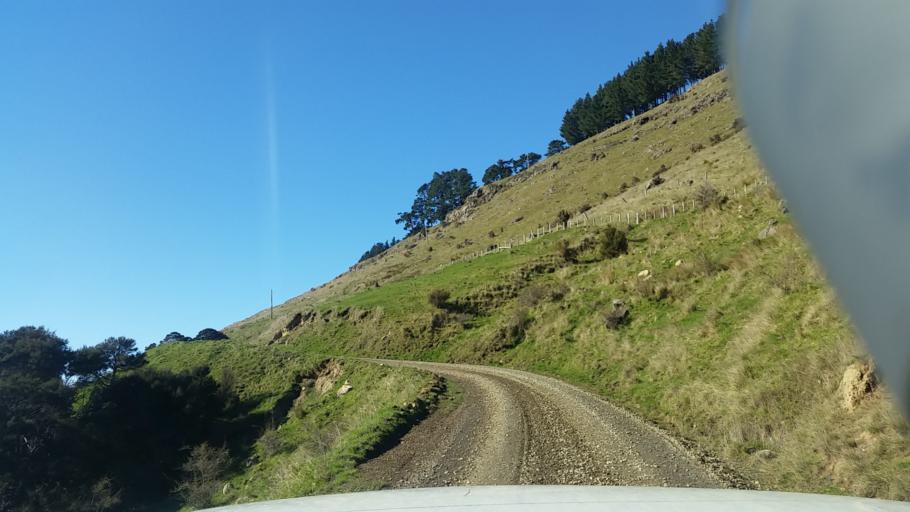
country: NZ
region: Canterbury
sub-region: Christchurch City
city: Christchurch
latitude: -43.6641
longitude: 172.9844
